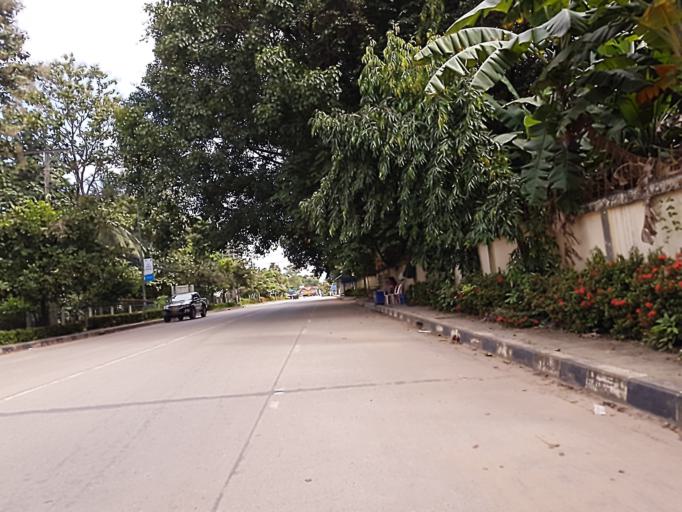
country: LA
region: Vientiane
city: Vientiane
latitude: 17.9385
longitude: 102.6242
